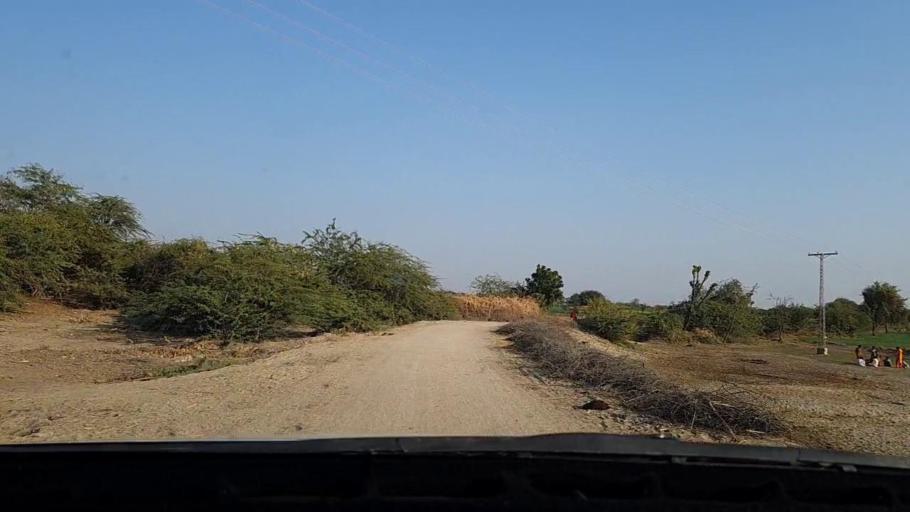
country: PK
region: Sindh
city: Tando Mittha Khan
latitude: 25.8581
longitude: 69.3145
